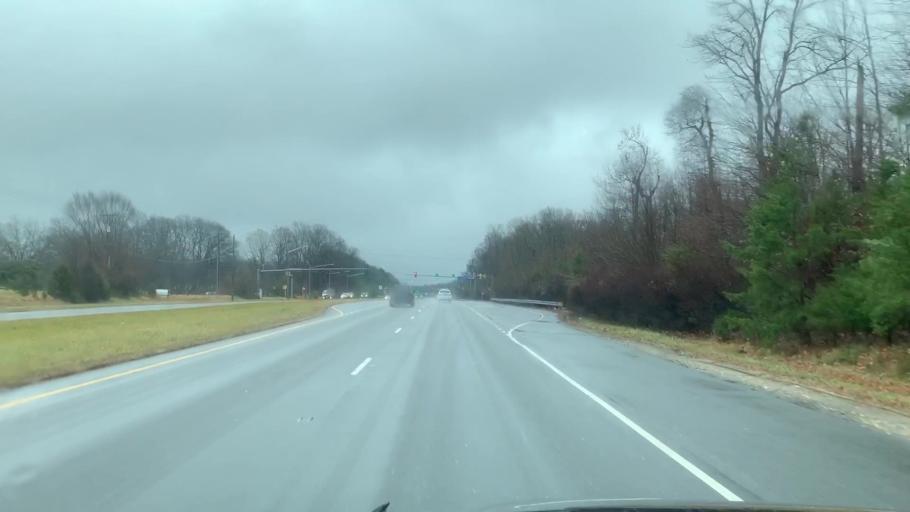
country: US
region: Virginia
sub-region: Fairfax County
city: Fairfax Station
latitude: 38.7638
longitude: -77.3114
